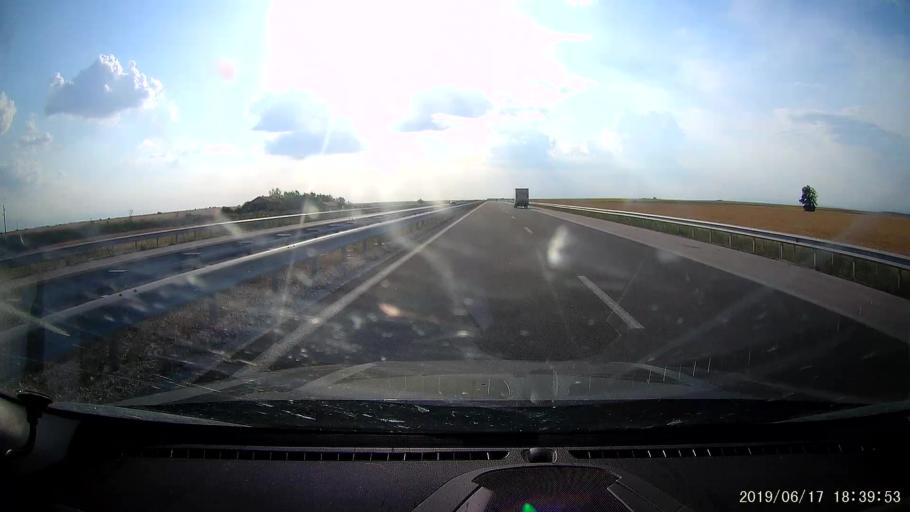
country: BG
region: Stara Zagora
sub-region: Obshtina Chirpan
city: Chirpan
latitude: 42.1495
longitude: 25.2938
